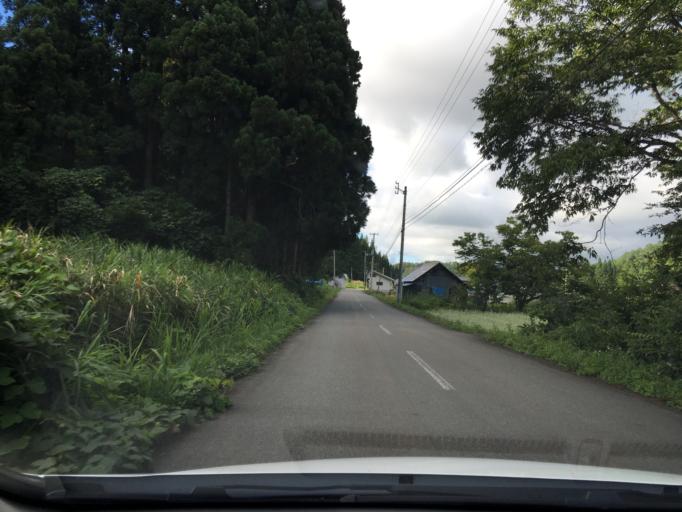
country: JP
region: Yamagata
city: Yonezawa
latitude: 37.9149
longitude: 140.2037
